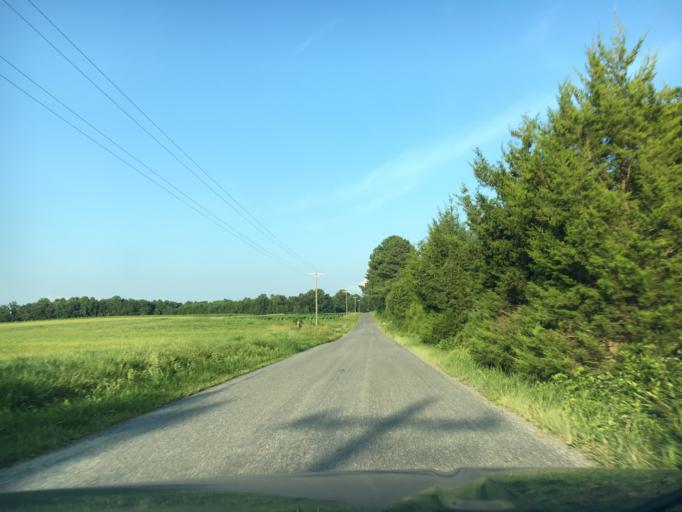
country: US
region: Virginia
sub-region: Pittsylvania County
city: Gretna
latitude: 36.8418
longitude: -79.1959
